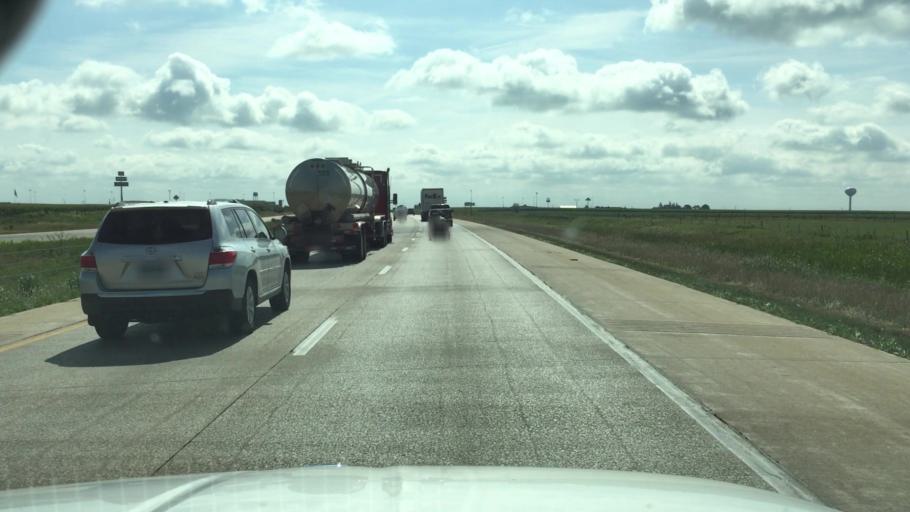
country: US
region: Iowa
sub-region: Scott County
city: Walcott
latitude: 41.6194
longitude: -90.7976
